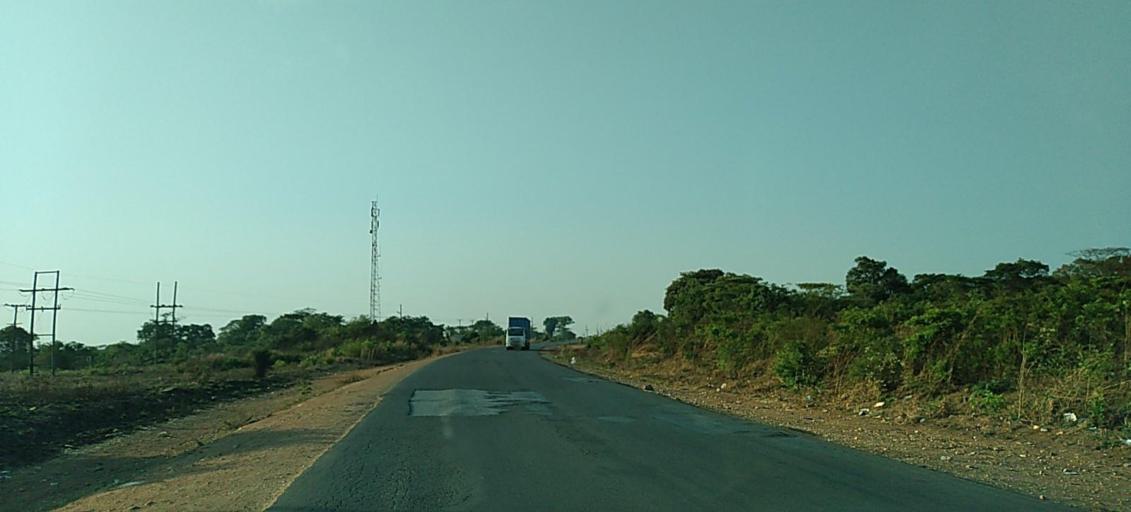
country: ZM
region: Copperbelt
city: Luanshya
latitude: -13.3081
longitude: 28.6885
